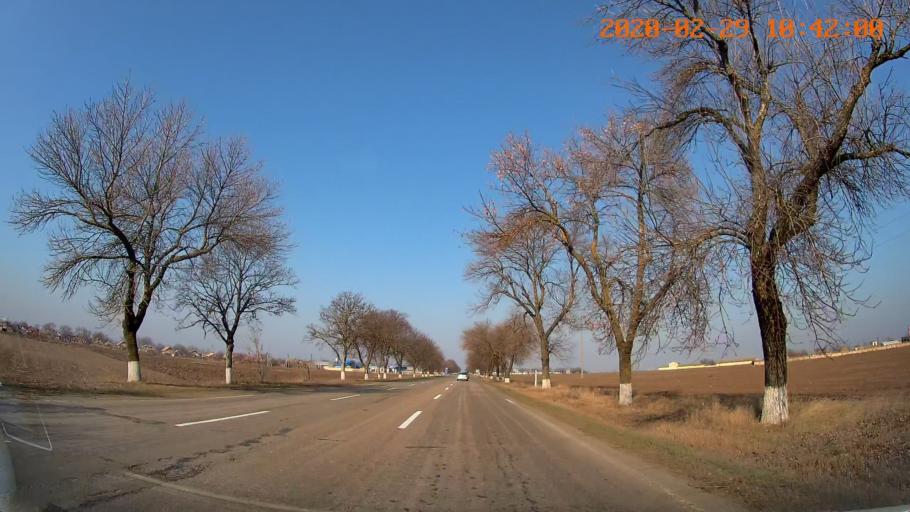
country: MD
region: Telenesti
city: Grigoriopol
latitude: 47.0476
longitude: 29.4171
